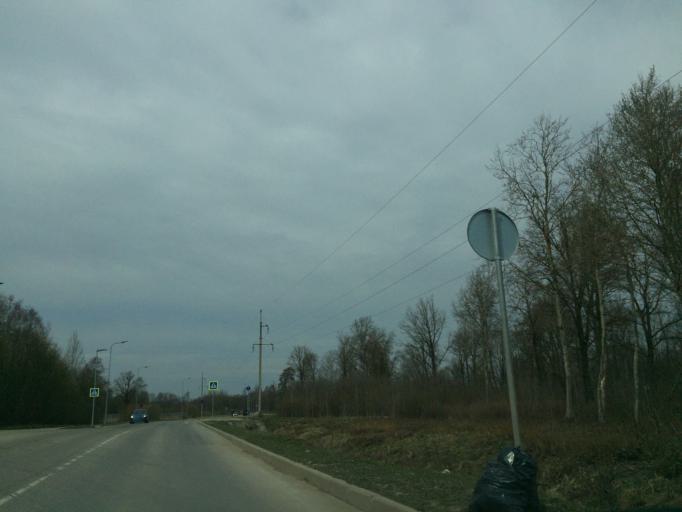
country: EE
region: Ida-Virumaa
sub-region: Narva linn
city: Narva
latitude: 59.3959
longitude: 28.1793
